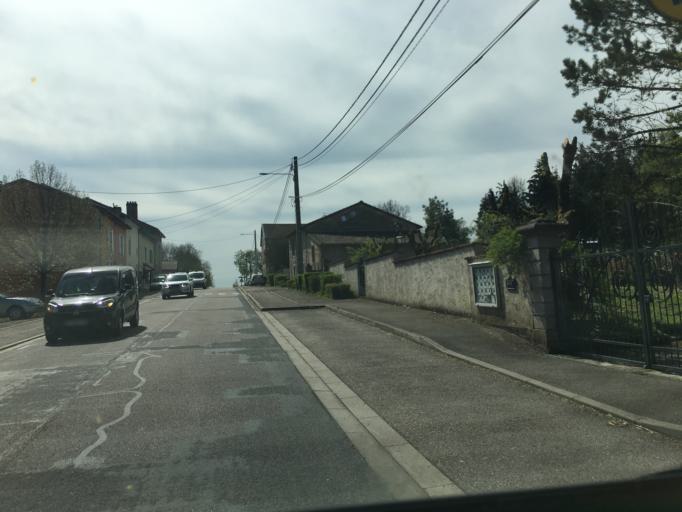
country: FR
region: Lorraine
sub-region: Departement de la Meuse
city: Lerouville
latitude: 48.8288
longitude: 5.5090
